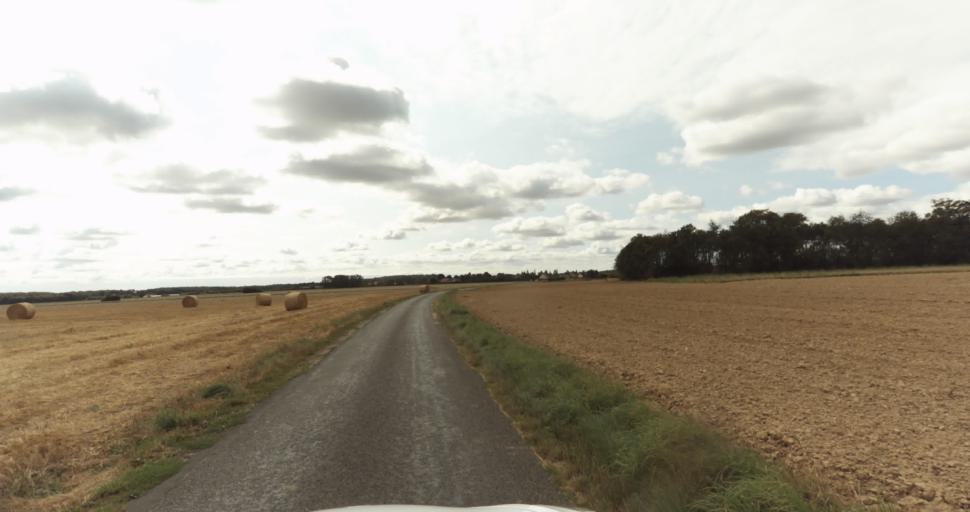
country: FR
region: Haute-Normandie
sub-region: Departement de l'Eure
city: Tillieres-sur-Avre
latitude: 48.7873
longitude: 1.1016
